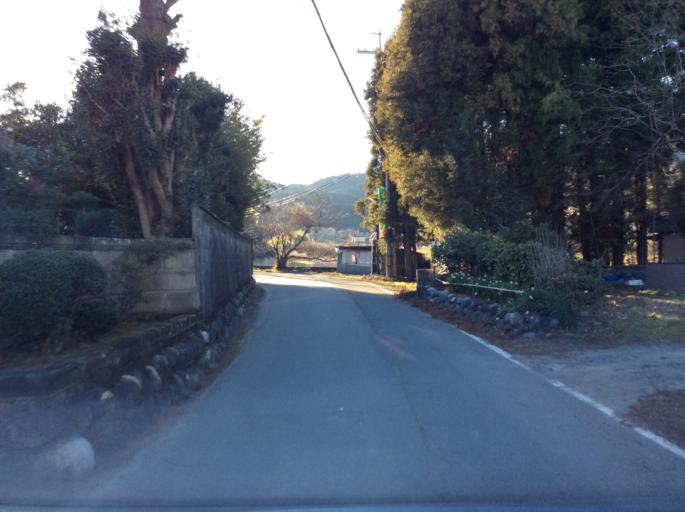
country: JP
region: Ibaraki
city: Kitaibaraki
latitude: 36.9052
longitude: 140.7336
